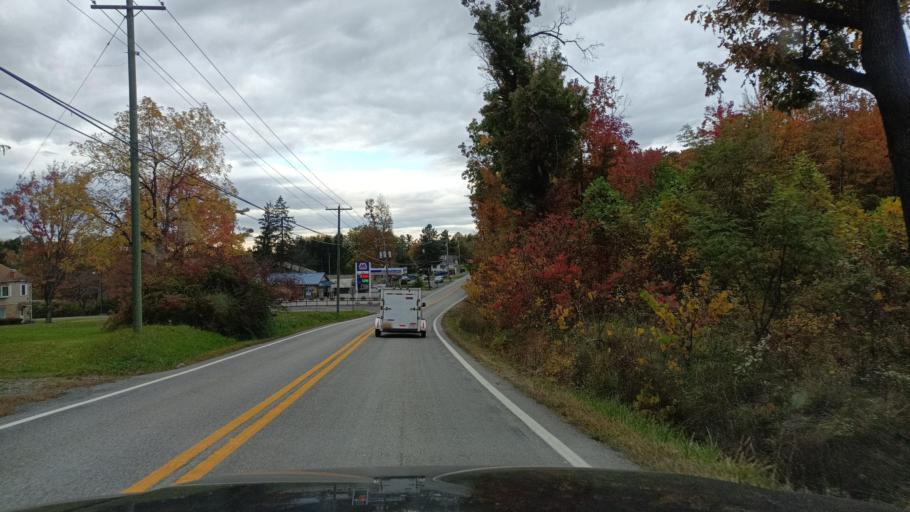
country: US
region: West Virginia
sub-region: Monongalia County
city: Brookhaven
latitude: 39.5641
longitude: -79.9439
